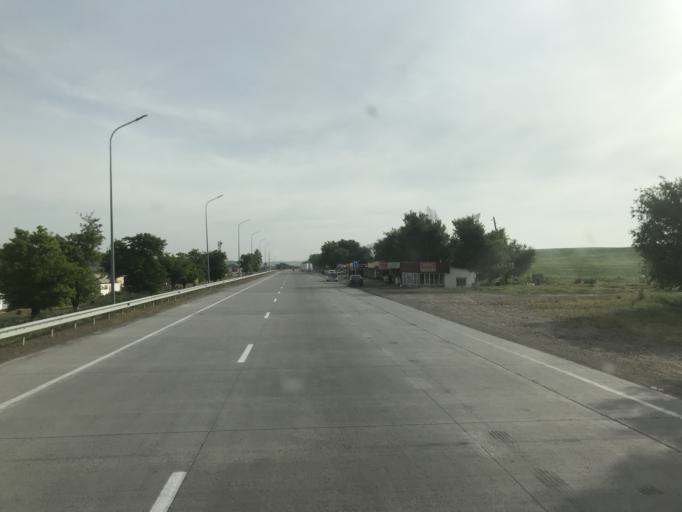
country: KZ
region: Ongtustik Qazaqstan
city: Qazyqurt
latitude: 41.9028
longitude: 69.4624
